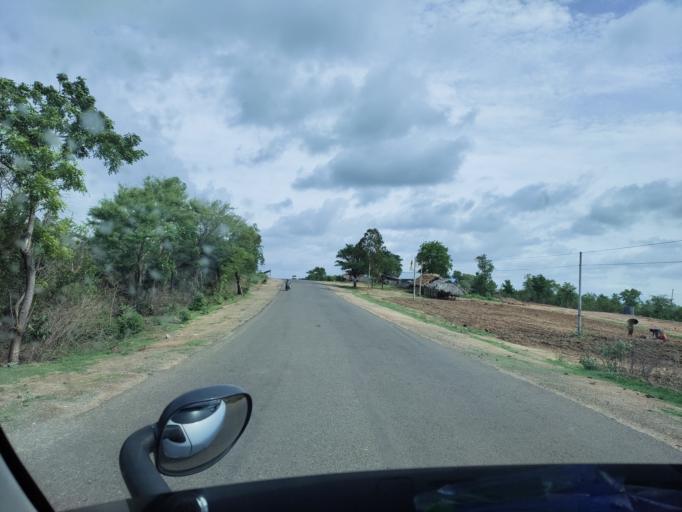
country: MM
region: Magway
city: Chauk
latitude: 20.9693
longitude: 95.0569
